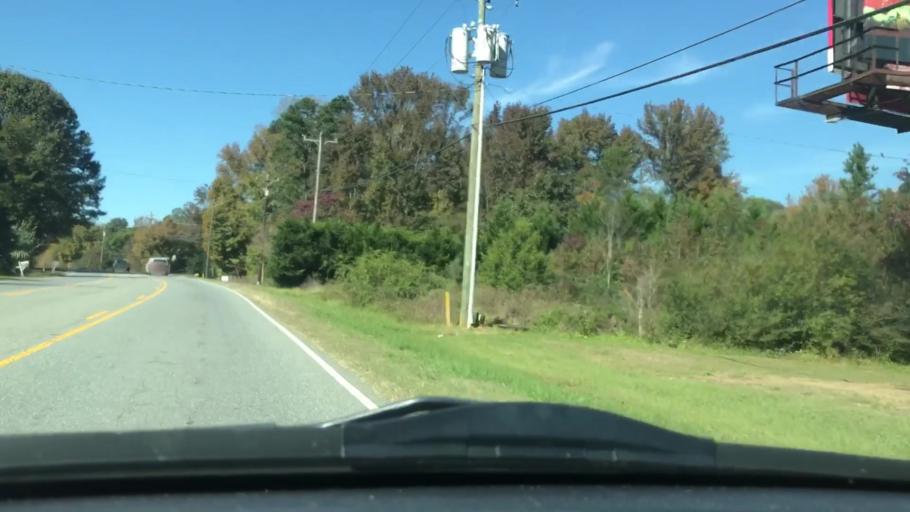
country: US
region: North Carolina
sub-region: Randolph County
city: Randleman
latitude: 35.8115
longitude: -79.8355
